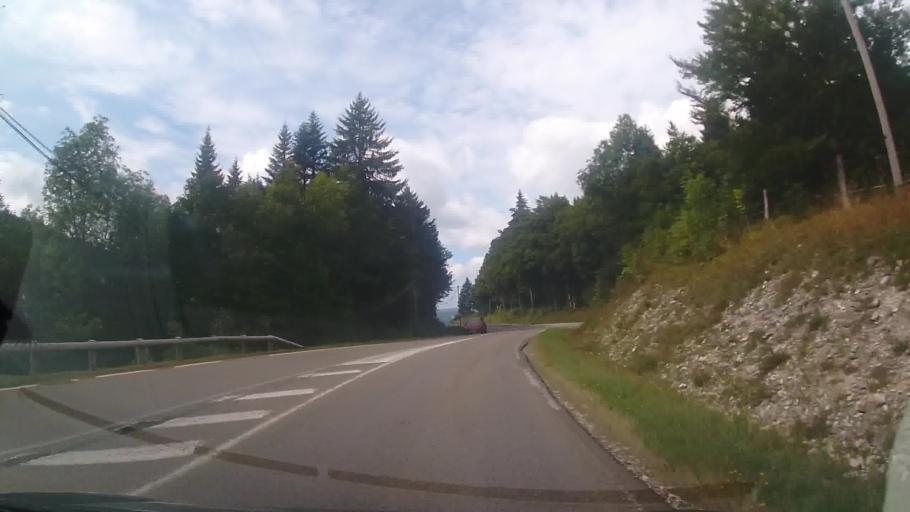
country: FR
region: Franche-Comte
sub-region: Departement du Jura
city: Les Rousses
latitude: 46.4494
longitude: 6.0751
